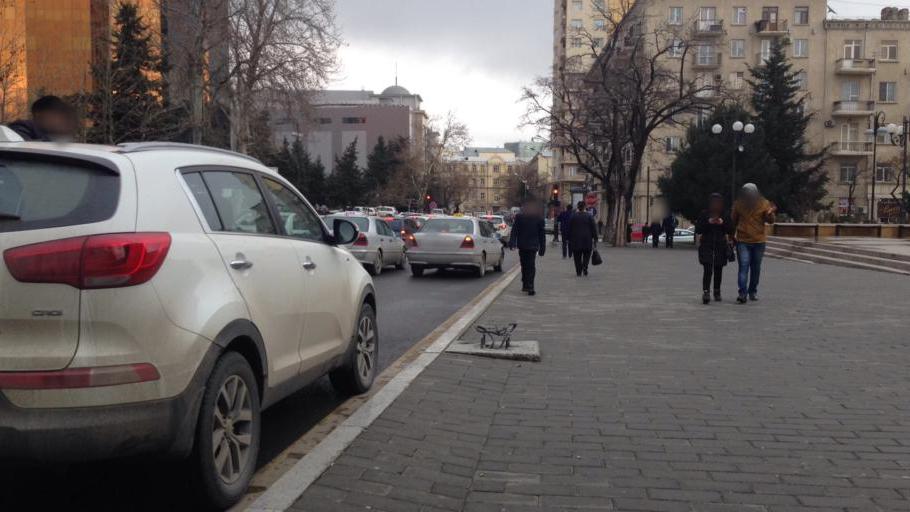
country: AZ
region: Baki
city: Baku
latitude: 40.3777
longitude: 49.8441
